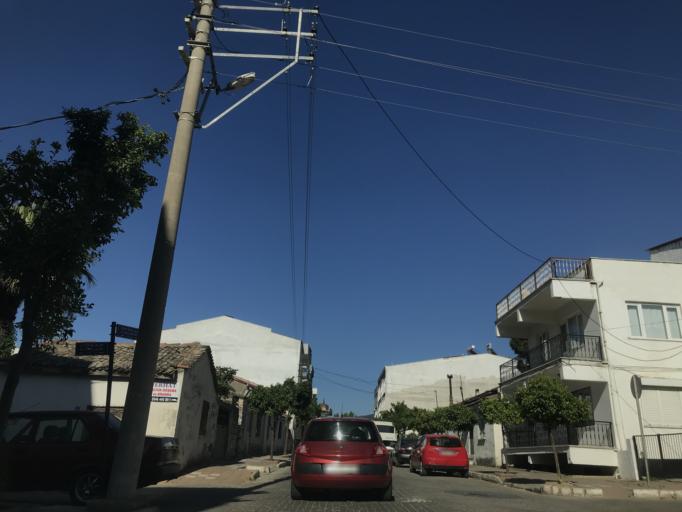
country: TR
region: Aydin
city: Davutlar
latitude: 37.7328
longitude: 27.2897
